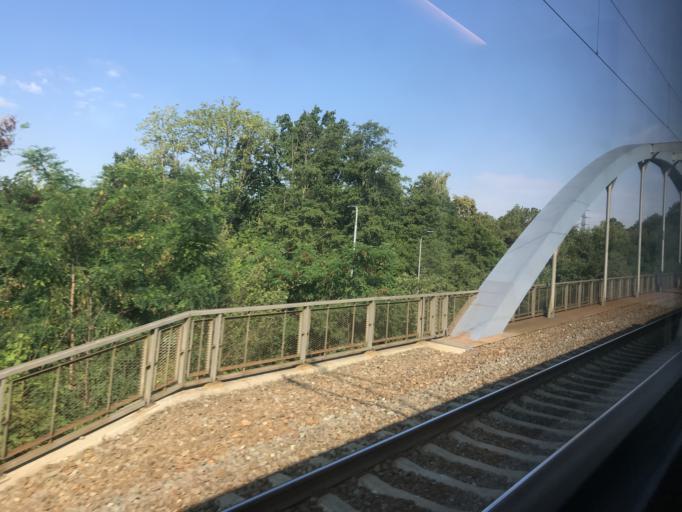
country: CZ
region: Jihocesky
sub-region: Okres Tabor
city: Sezimovo Usti
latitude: 49.3979
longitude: 14.6874
